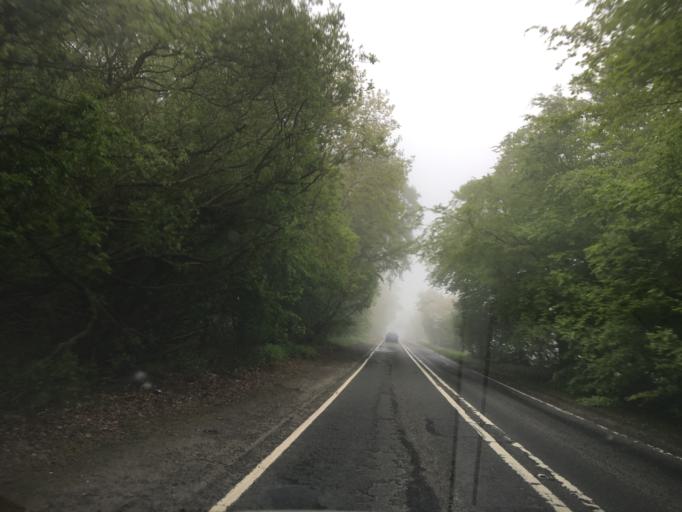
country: GB
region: Scotland
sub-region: Midlothian
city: Penicuik
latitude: 55.8191
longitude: -3.2021
